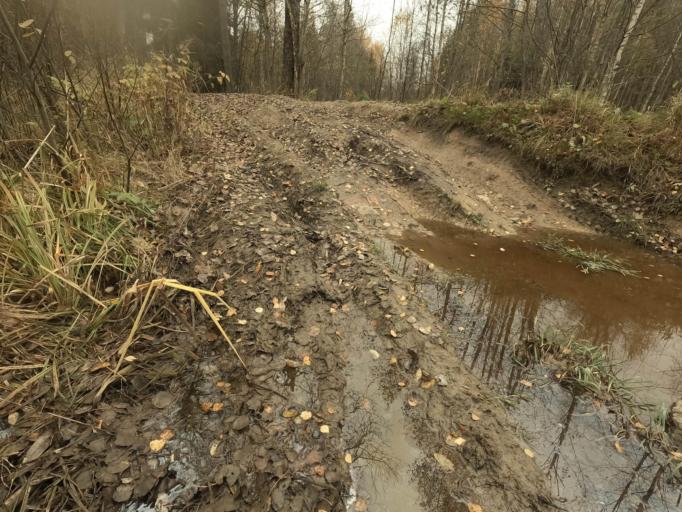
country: RU
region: Leningrad
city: Pavlovo
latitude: 59.7709
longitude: 30.9127
